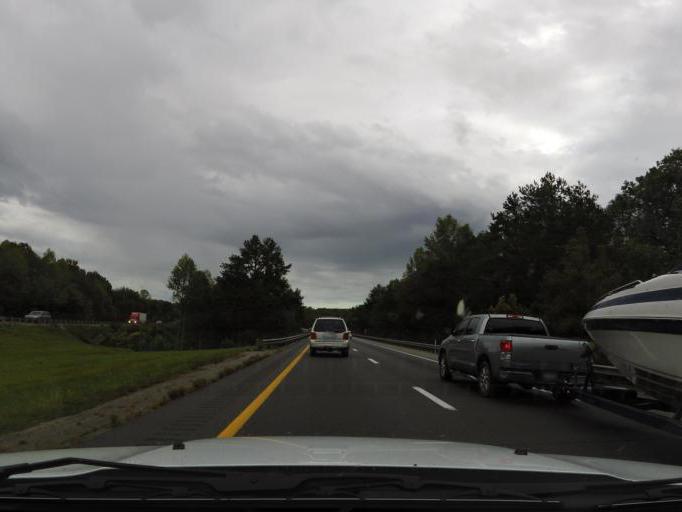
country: US
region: Kentucky
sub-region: Laurel County
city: North Corbin
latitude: 37.0200
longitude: -84.0995
